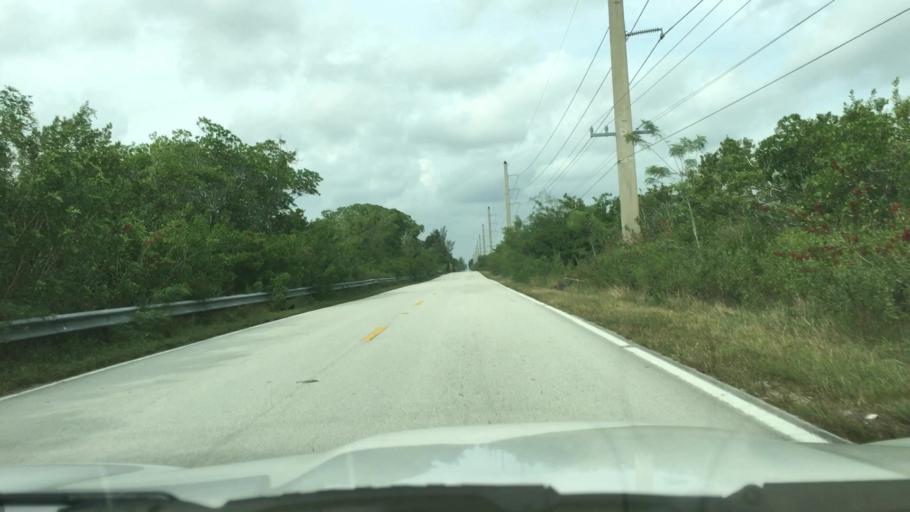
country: US
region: Florida
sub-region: Monroe County
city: North Key Largo
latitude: 25.3280
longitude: -80.4045
